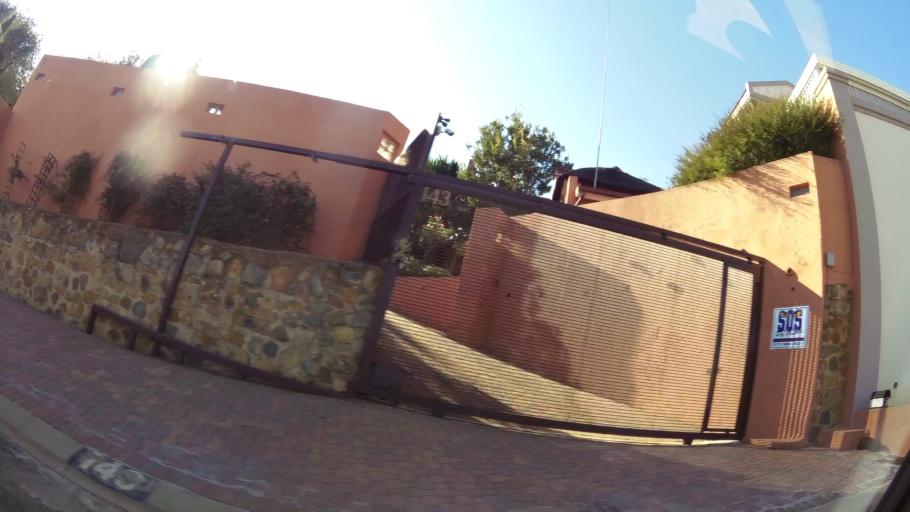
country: ZA
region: Gauteng
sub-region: City of Johannesburg Metropolitan Municipality
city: Johannesburg
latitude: -26.2821
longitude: 28.0500
